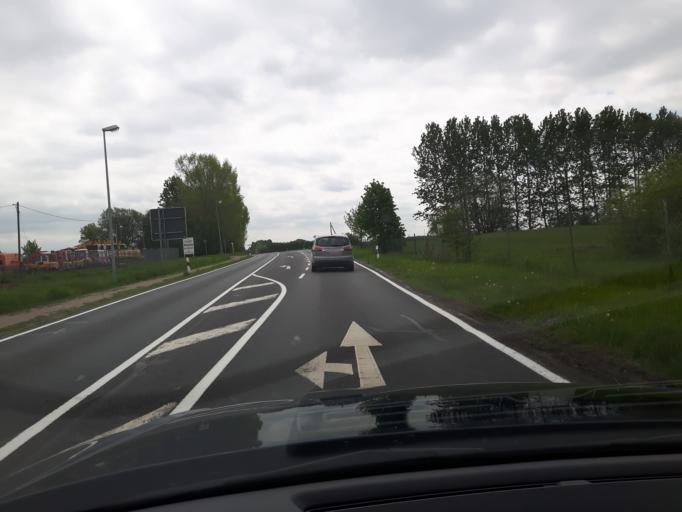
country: DE
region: Mecklenburg-Vorpommern
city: Ostseebad Dierhagen
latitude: 54.2403
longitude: 12.3619
